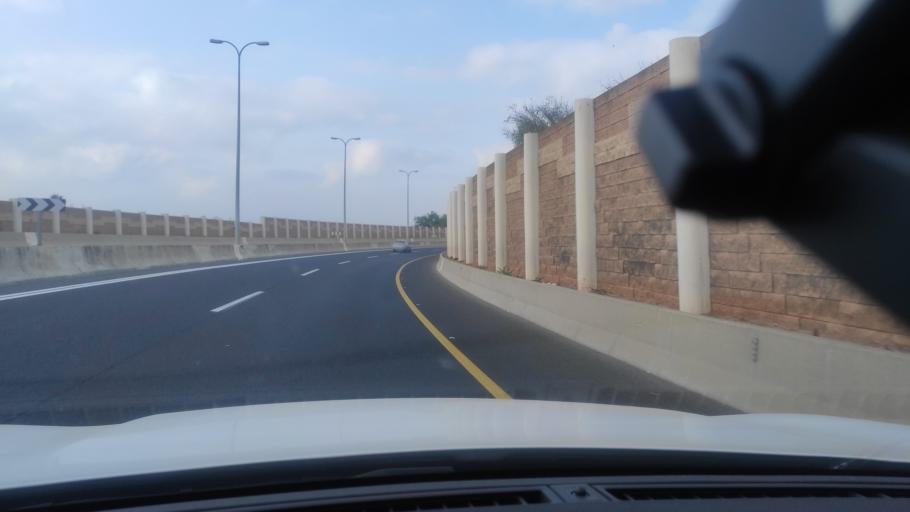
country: IL
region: Central District
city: Kfar Saba
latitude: 32.1587
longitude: 34.9264
